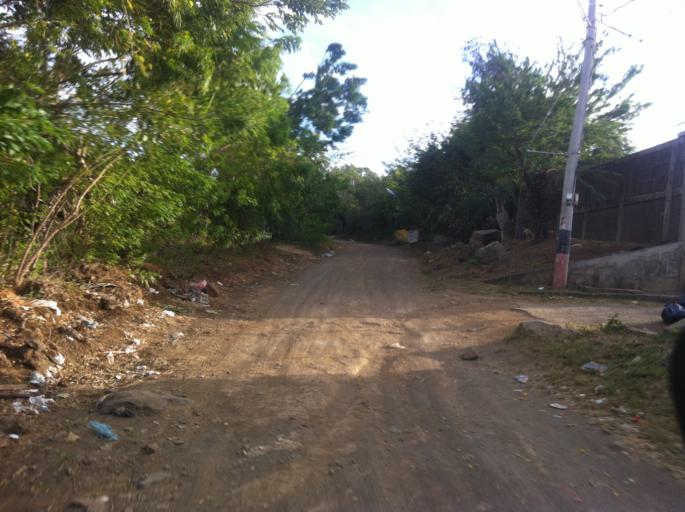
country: NI
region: Managua
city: Ciudad Sandino
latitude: 12.0945
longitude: -86.3137
